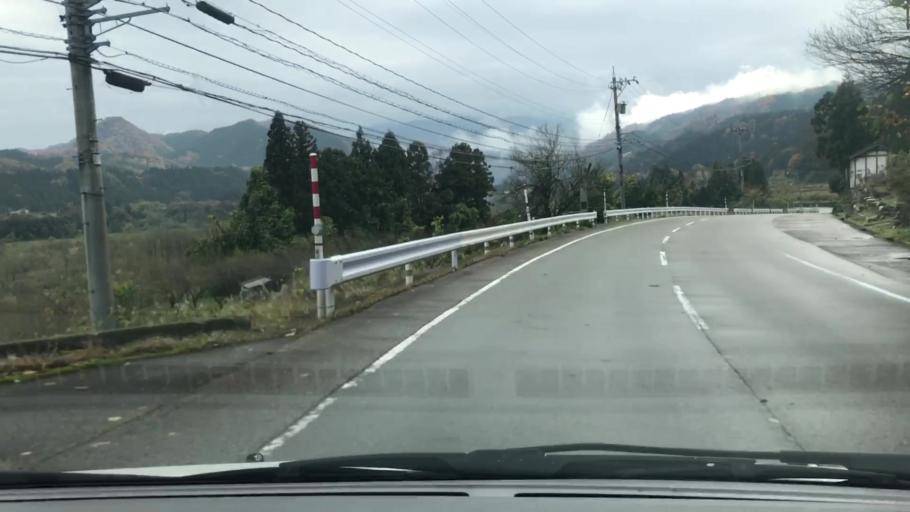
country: JP
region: Toyama
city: Kamiichi
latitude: 36.5913
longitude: 137.3174
